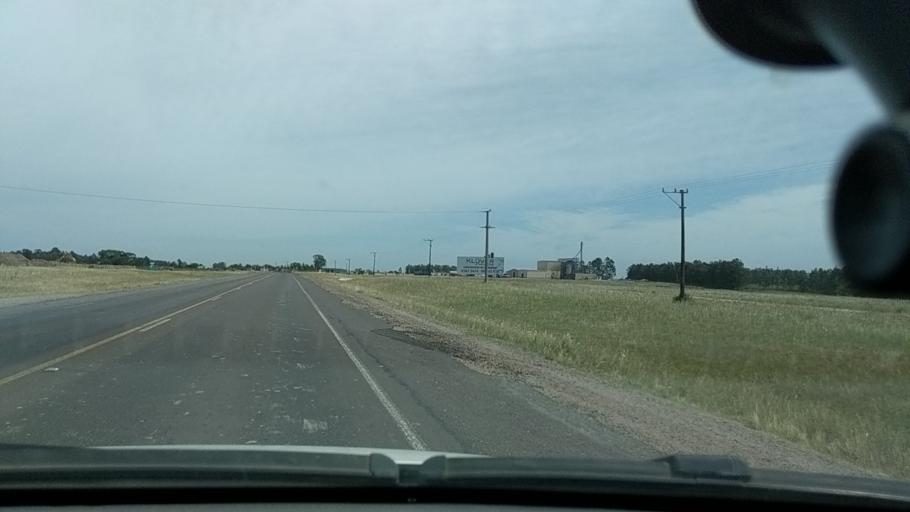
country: UY
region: Durazno
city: Durazno
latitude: -33.4479
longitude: -56.4753
